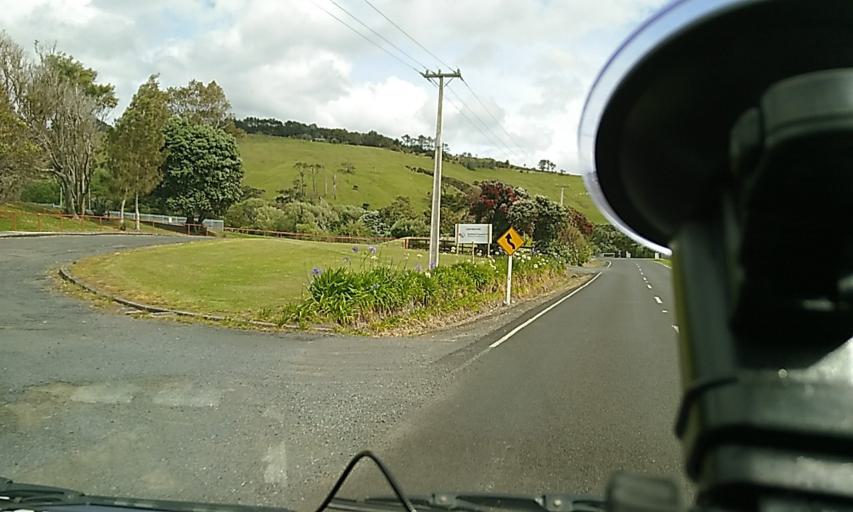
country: NZ
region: Northland
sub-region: Far North District
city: Ahipara
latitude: -35.5292
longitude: 173.3898
